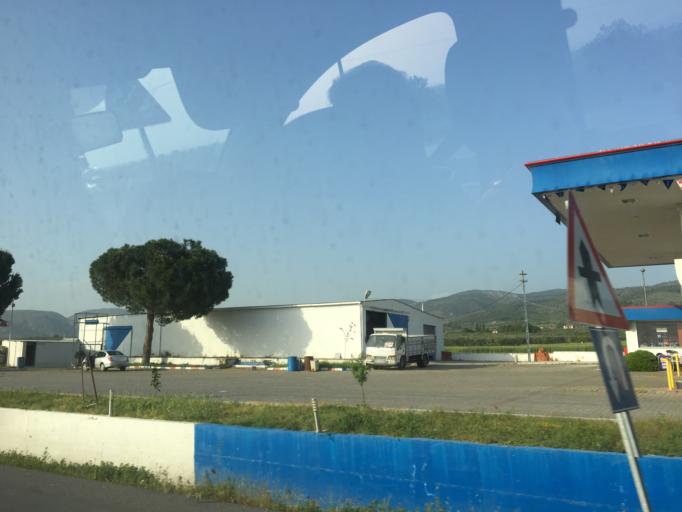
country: TR
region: Manisa
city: Golmarmara
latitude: 38.7897
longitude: 27.9018
